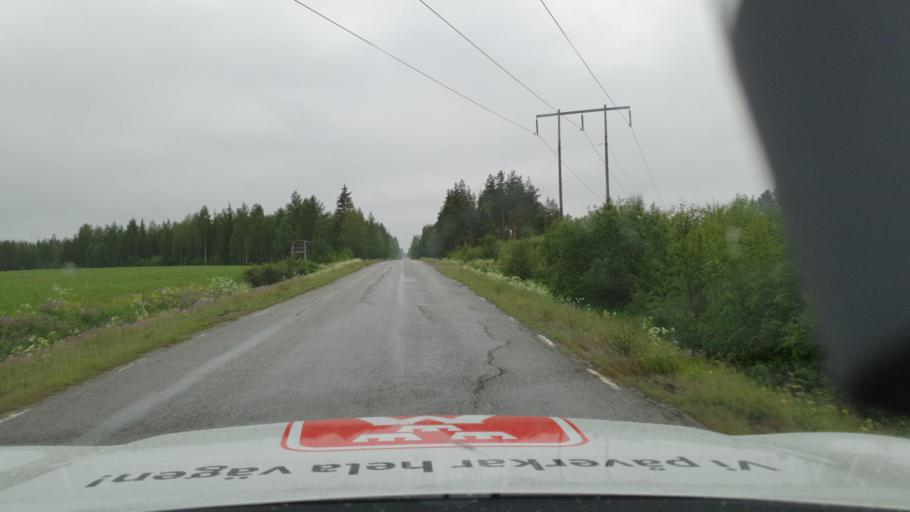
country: SE
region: Vaesterbotten
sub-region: Nordmalings Kommun
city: Nordmaling
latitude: 63.8138
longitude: 19.4984
